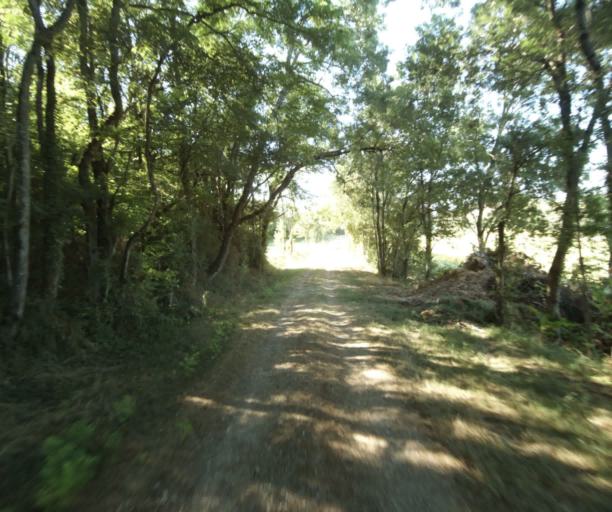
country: FR
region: Midi-Pyrenees
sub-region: Departement de la Haute-Garonne
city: Saint-Felix-Lauragais
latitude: 43.5144
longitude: 1.9310
